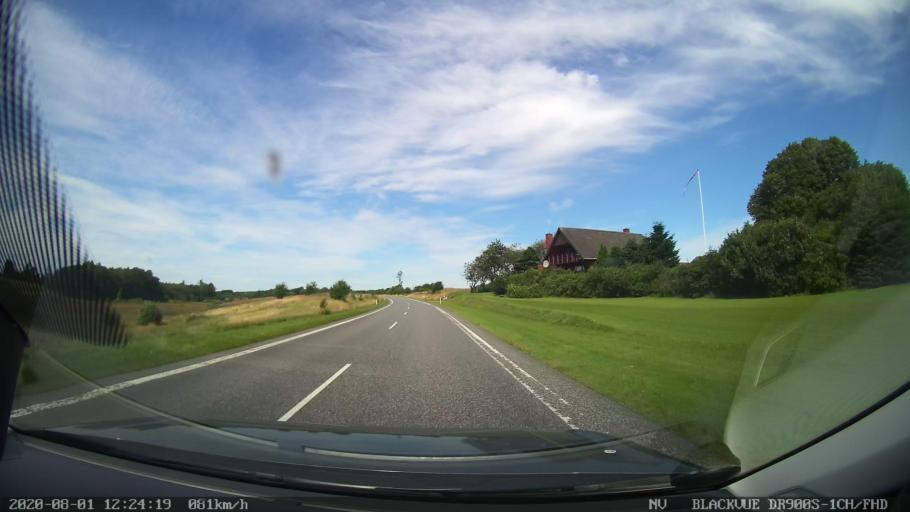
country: DK
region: Central Jutland
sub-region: Viborg Kommune
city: Stoholm
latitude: 56.4041
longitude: 9.1301
